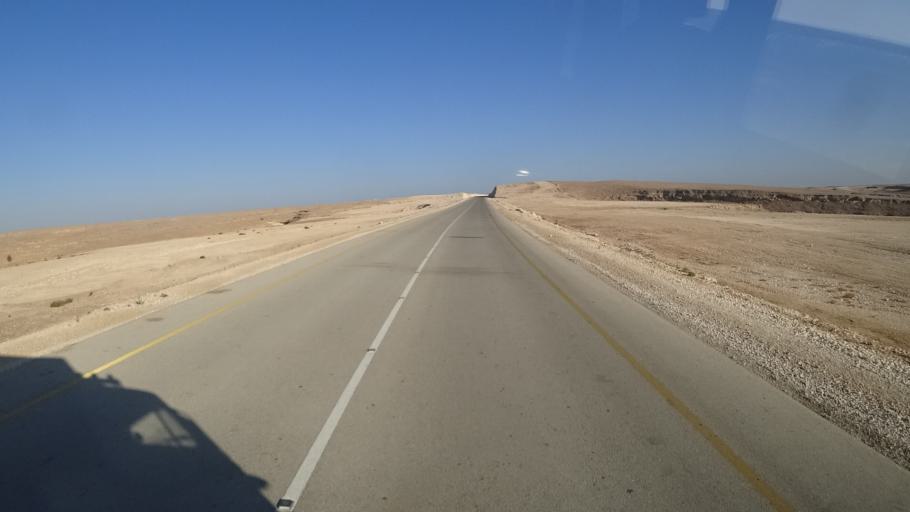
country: YE
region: Al Mahrah
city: Hawf
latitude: 17.0867
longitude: 53.0781
